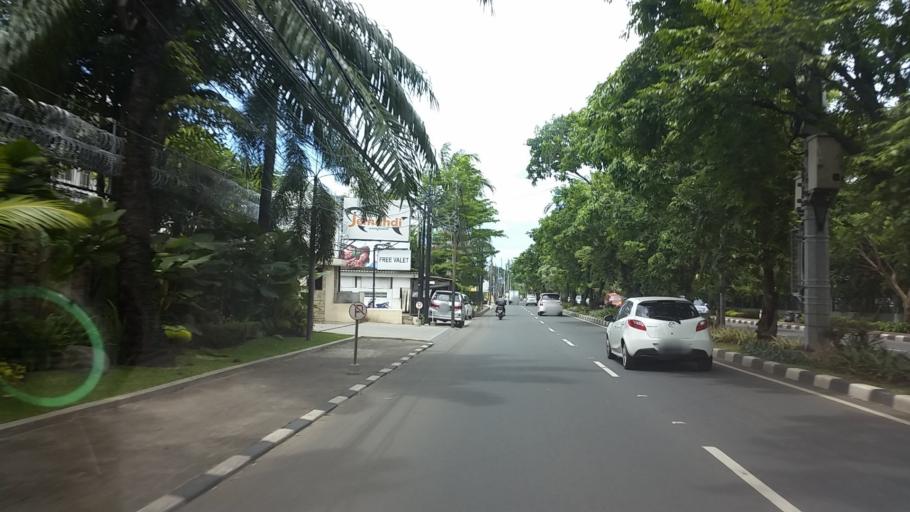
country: ID
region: Jakarta Raya
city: Jakarta
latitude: -6.1209
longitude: 106.7941
